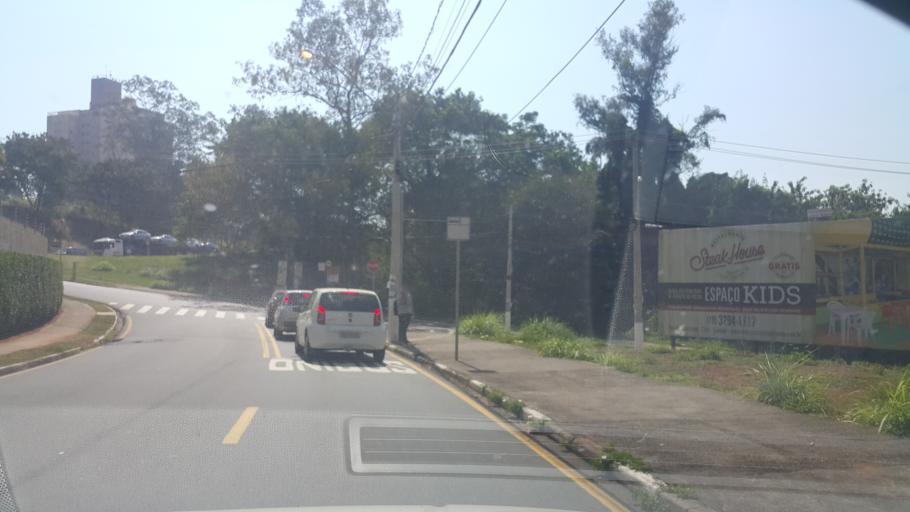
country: BR
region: Sao Paulo
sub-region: Campinas
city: Campinas
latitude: -22.8535
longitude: -47.0482
